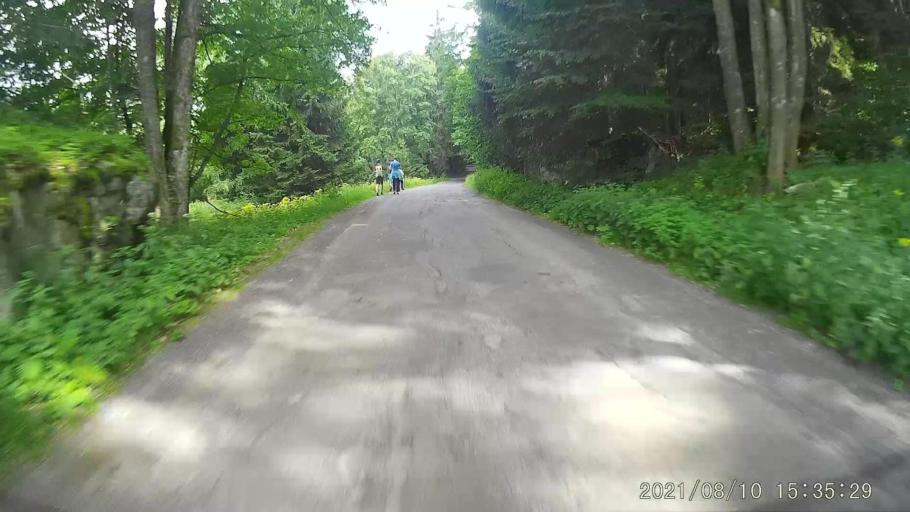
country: PL
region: Lower Silesian Voivodeship
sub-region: Powiat klodzki
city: Radkow
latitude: 50.4870
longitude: 16.3487
